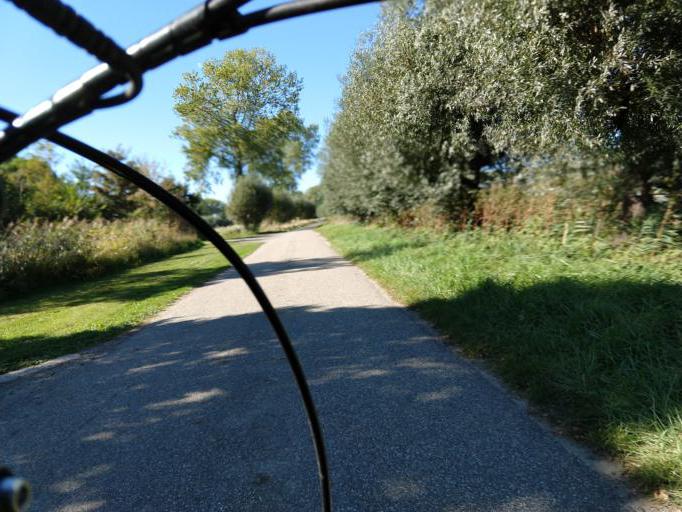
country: NL
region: Zeeland
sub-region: Gemeente Goes
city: Goes
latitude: 51.4414
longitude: 3.8468
